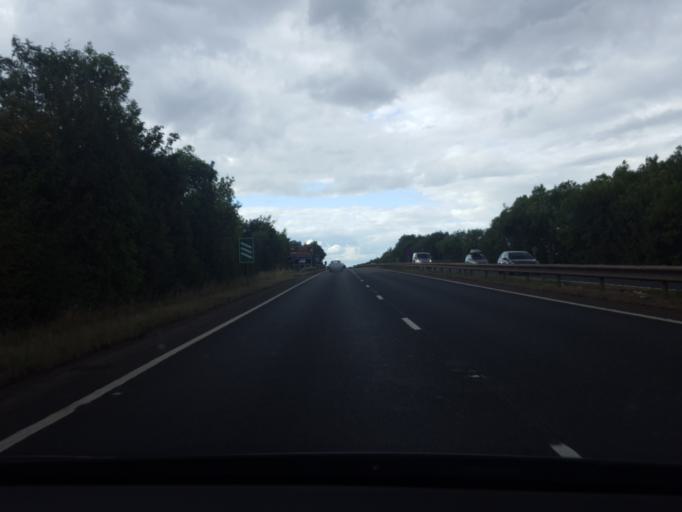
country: GB
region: England
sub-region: Leicestershire
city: Mountsorrel
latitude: 52.7308
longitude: -1.1333
